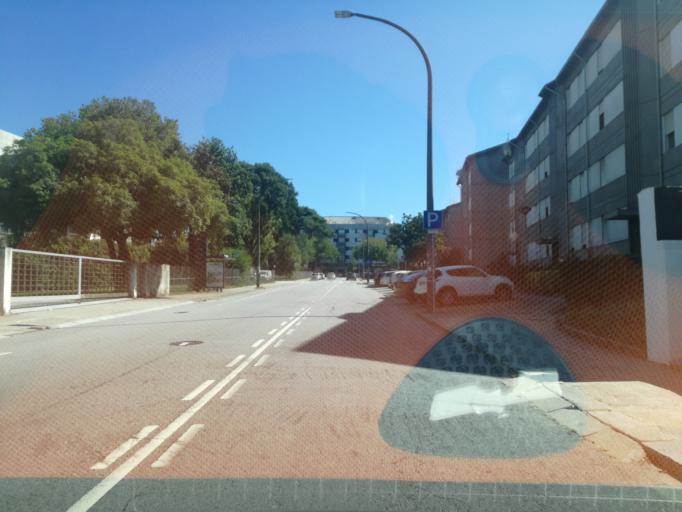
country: PT
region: Porto
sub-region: Matosinhos
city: Sao Mamede de Infesta
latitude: 41.1790
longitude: -8.6093
